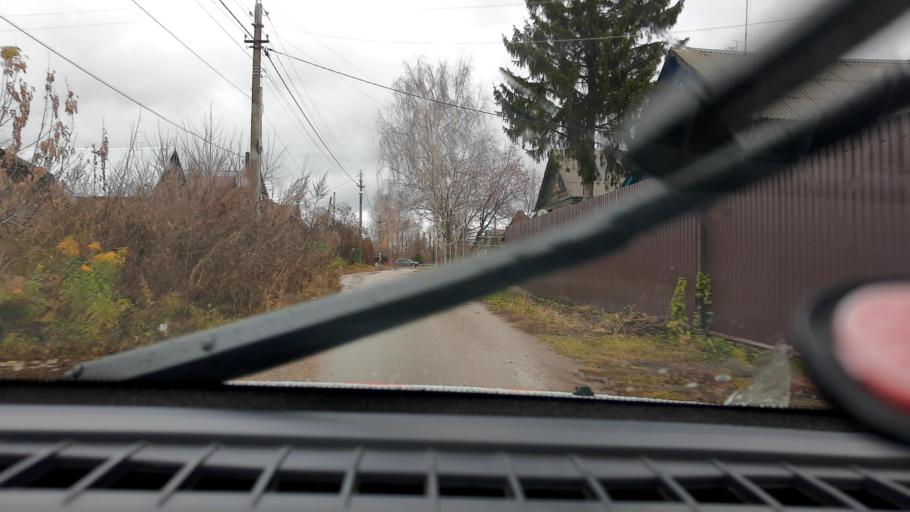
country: RU
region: Nizjnij Novgorod
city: Afonino
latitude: 56.2717
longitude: 44.1071
